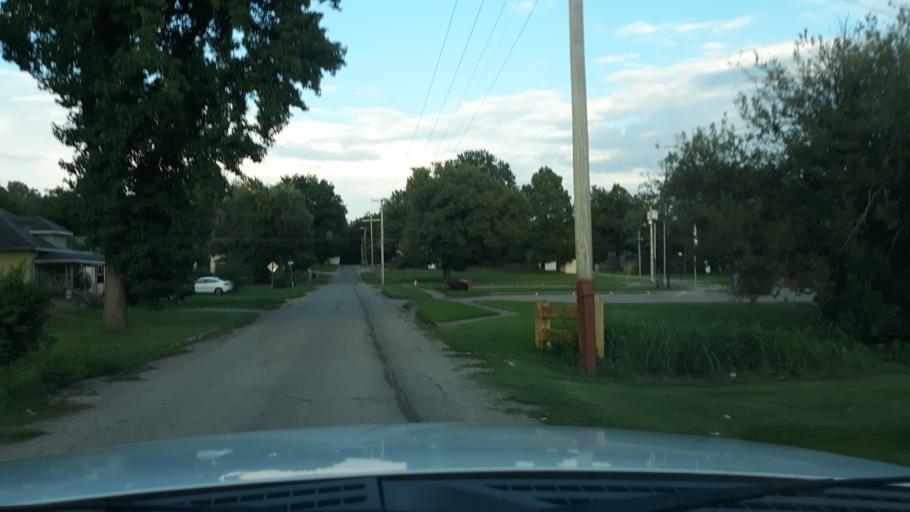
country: US
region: Illinois
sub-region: Saline County
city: Eldorado
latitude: 37.8152
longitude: -88.4366
